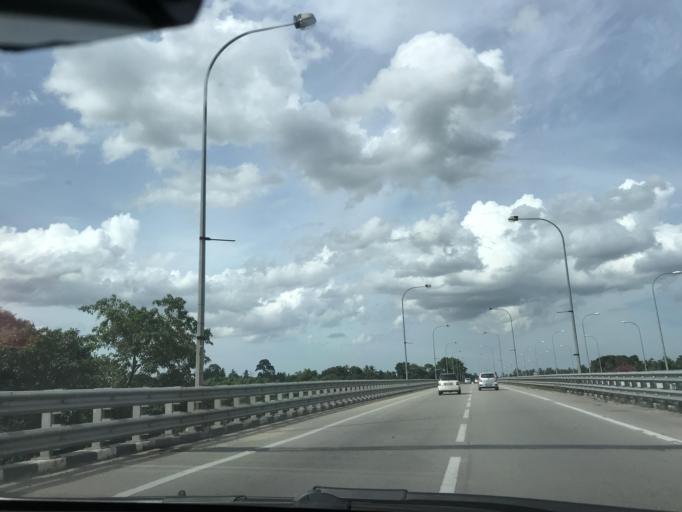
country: MY
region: Kelantan
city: Kampung Lemal
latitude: 6.0309
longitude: 102.1441
